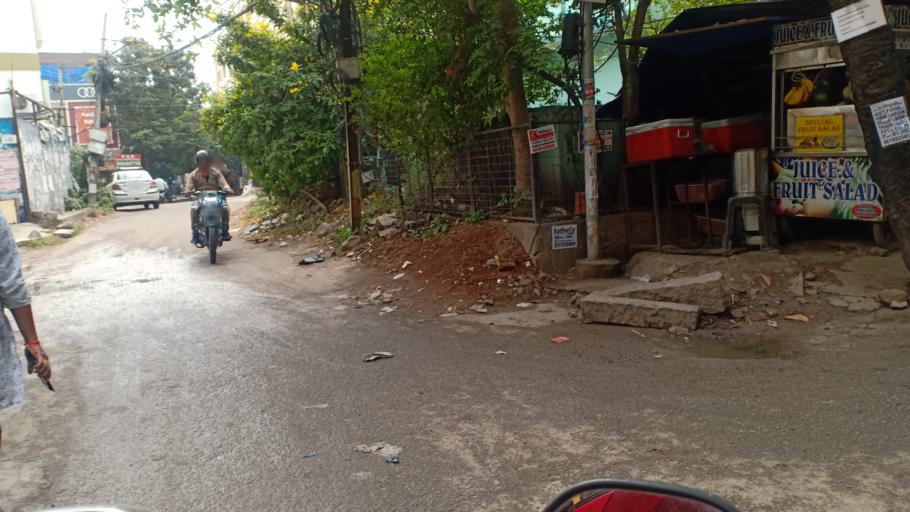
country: IN
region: Telangana
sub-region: Hyderabad
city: Hyderabad
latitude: 17.4352
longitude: 78.4408
